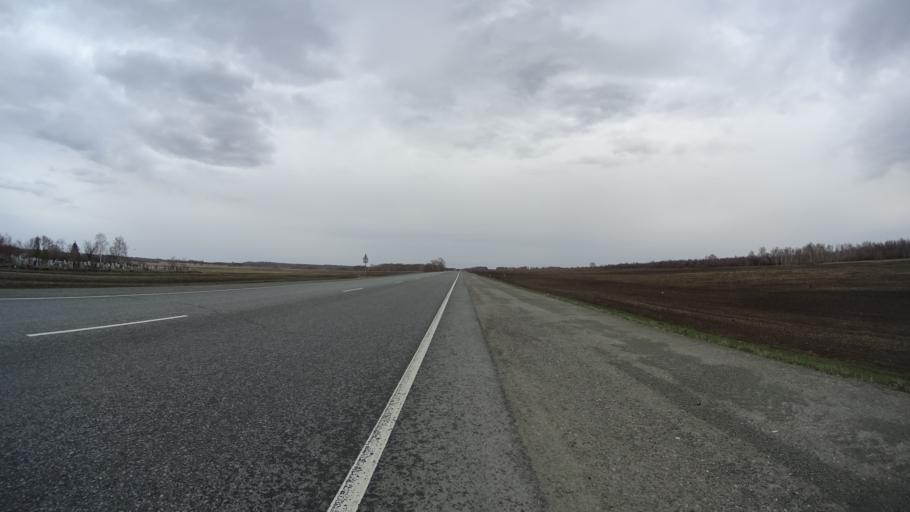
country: RU
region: Chelyabinsk
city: Krasnogorskiy
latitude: 54.6689
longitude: 61.2514
